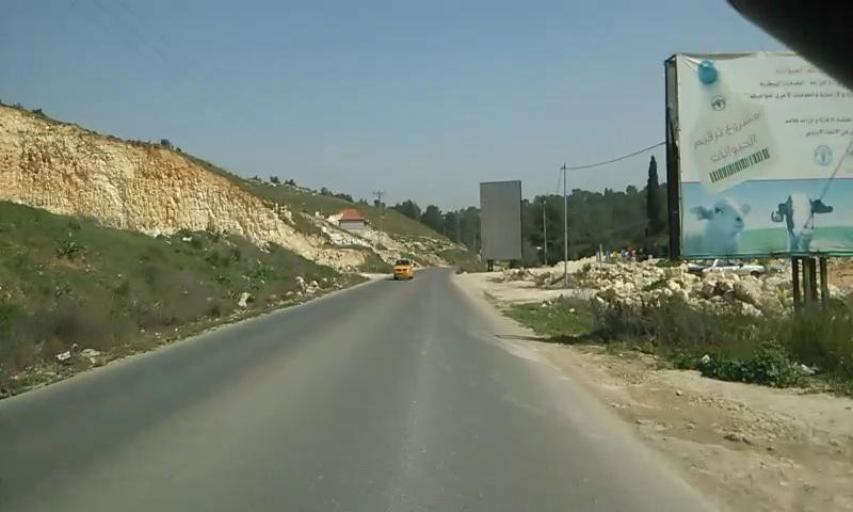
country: PS
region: West Bank
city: Ash Shuhada'
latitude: 32.4396
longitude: 35.2831
